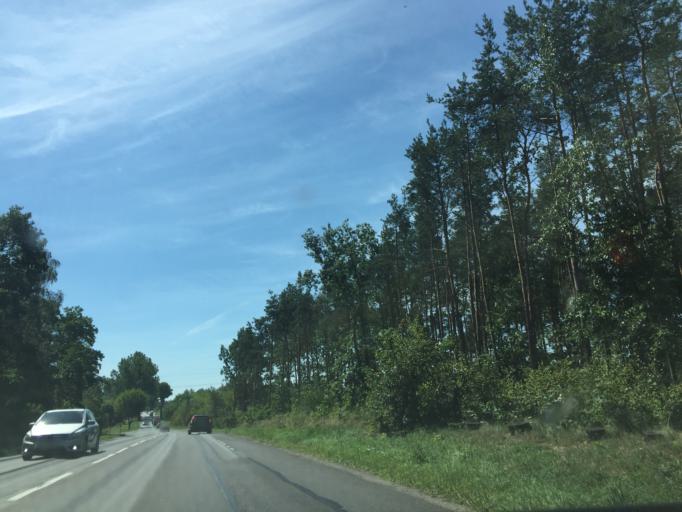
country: PL
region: Lodz Voivodeship
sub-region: Piotrkow Trybunalski
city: Piotrkow Trybunalski
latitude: 51.4254
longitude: 19.7140
